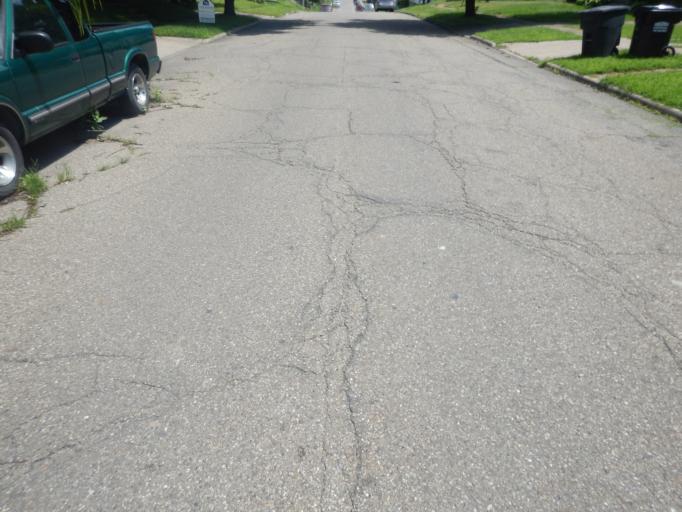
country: US
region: Ohio
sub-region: Muskingum County
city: Zanesville
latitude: 39.9560
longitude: -82.0073
